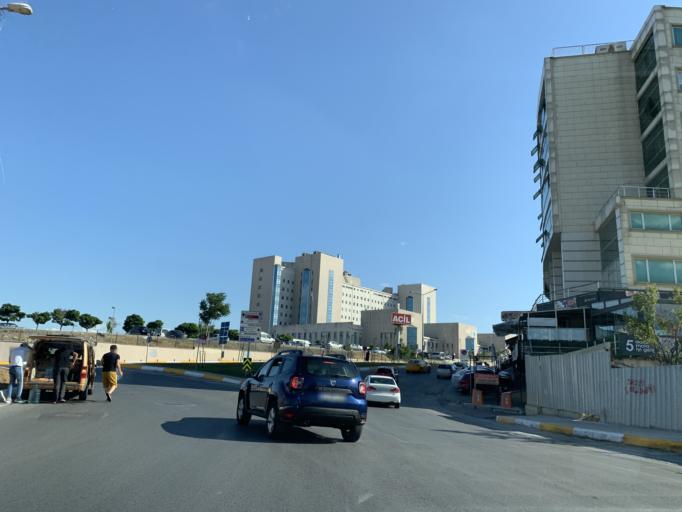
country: TR
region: Istanbul
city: Pendik
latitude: 40.8887
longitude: 29.2631
